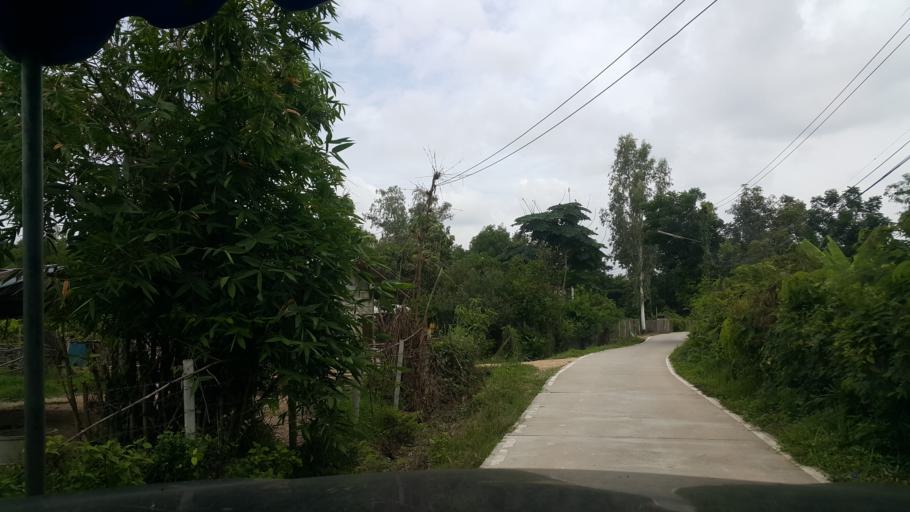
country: TH
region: Lamphun
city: Ban Thi
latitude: 18.6718
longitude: 99.1487
